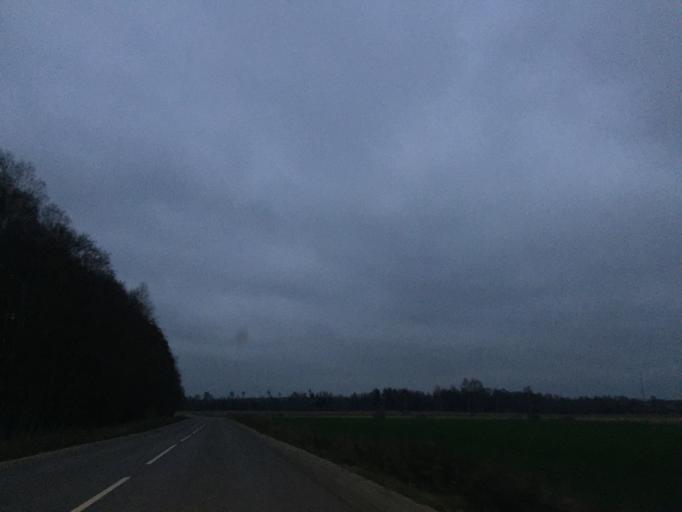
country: LV
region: Koceni
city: Koceni
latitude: 57.5510
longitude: 25.3425
